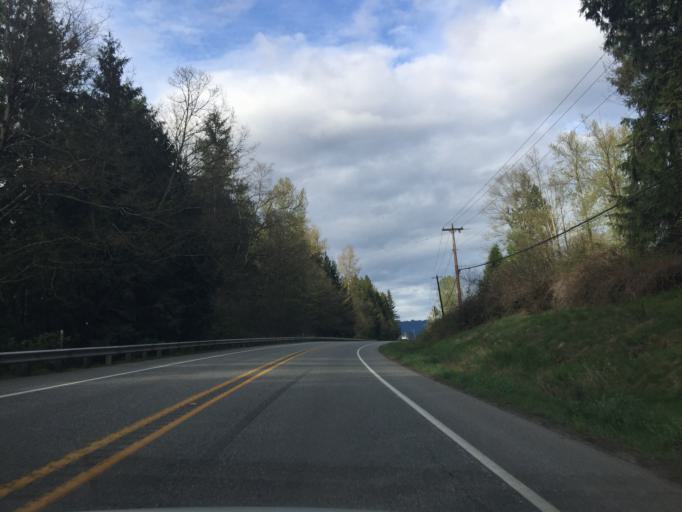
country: US
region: Washington
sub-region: Snohomish County
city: Arlington
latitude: 48.2147
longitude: -122.1120
